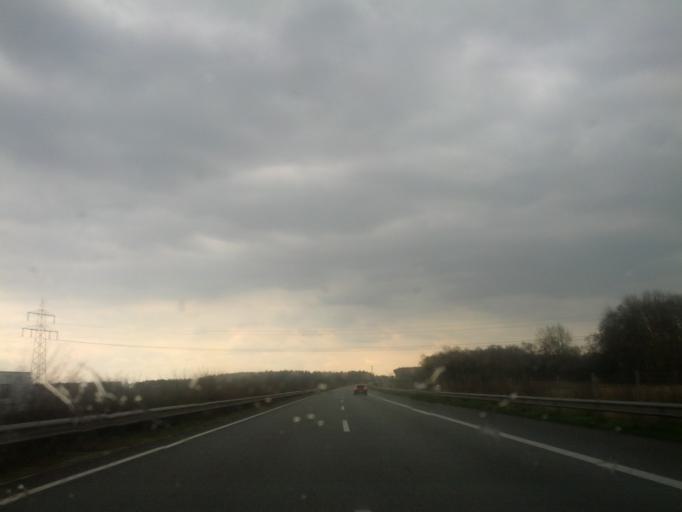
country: DE
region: Lower Saxony
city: Langwedel
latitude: 53.0108
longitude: 9.1470
